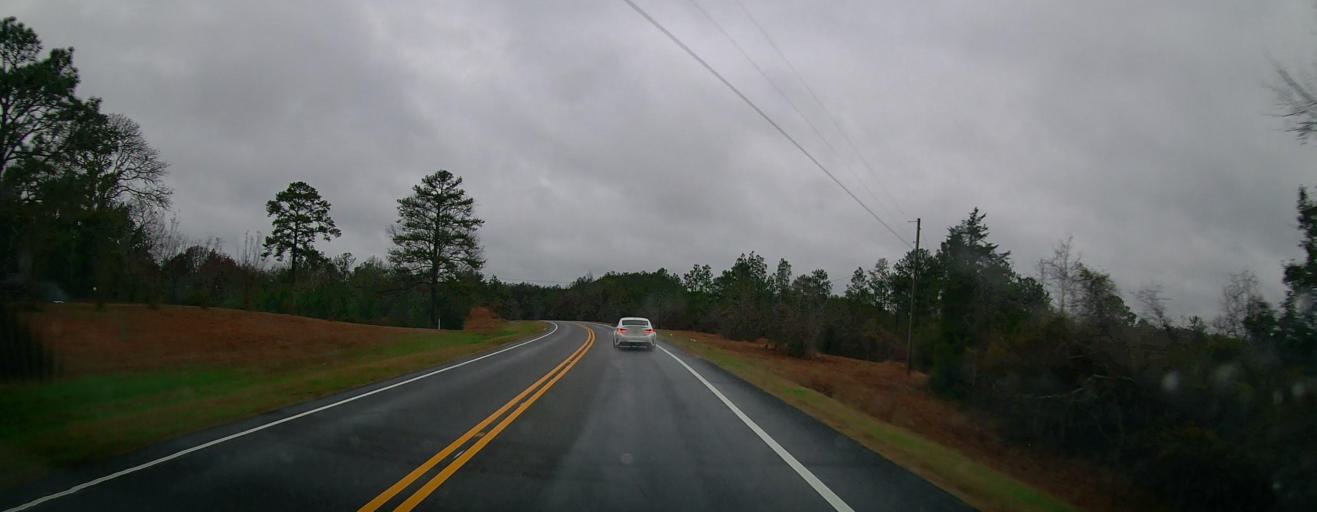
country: US
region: Alabama
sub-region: Chilton County
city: Clanton
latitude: 32.6665
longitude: -86.7750
